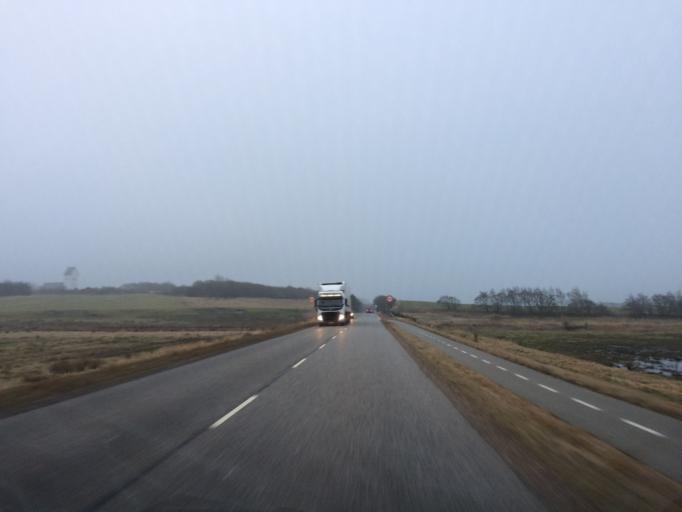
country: DK
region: Central Jutland
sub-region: Ringkobing-Skjern Kommune
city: Skjern
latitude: 55.9090
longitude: 8.4382
